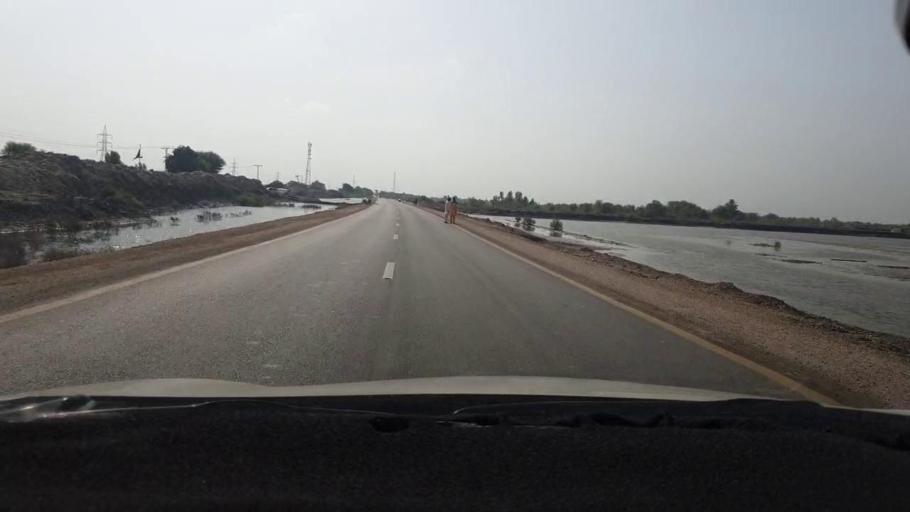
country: PK
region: Sindh
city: Jhol
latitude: 25.8901
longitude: 69.0309
